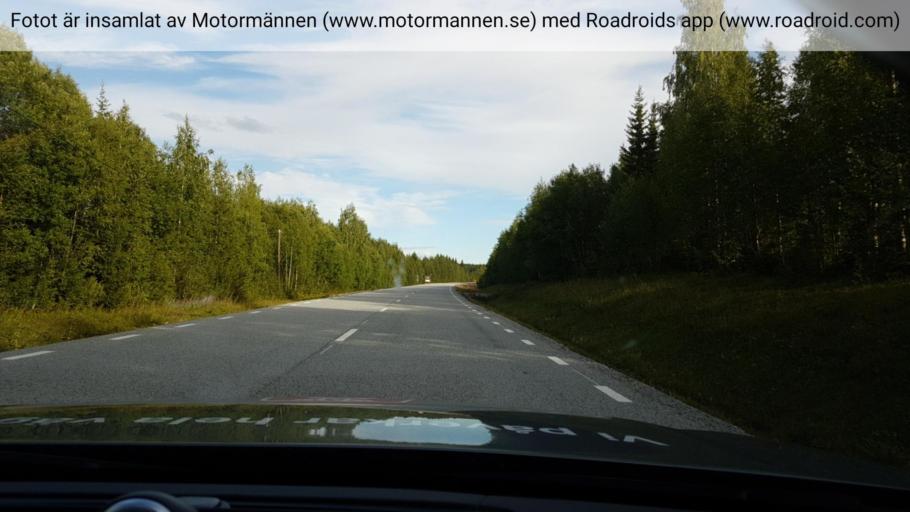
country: SE
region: Jaemtland
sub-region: Stroemsunds Kommun
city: Stroemsund
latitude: 64.2126
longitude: 15.5737
